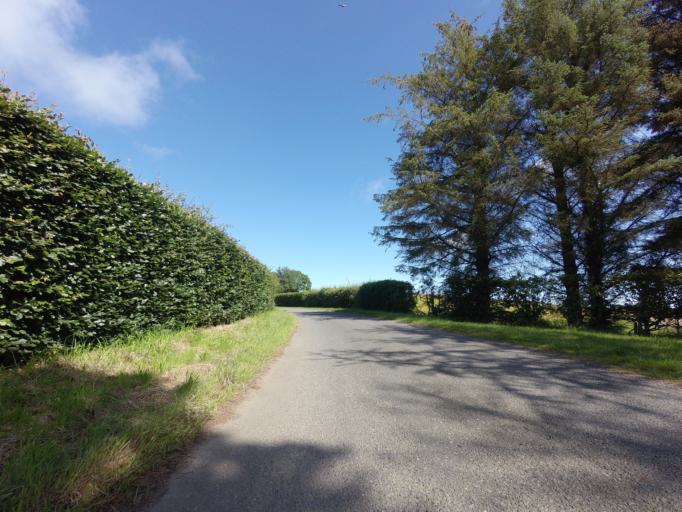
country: GB
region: Scotland
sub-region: Aberdeenshire
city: Banff
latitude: 57.6158
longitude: -2.5085
